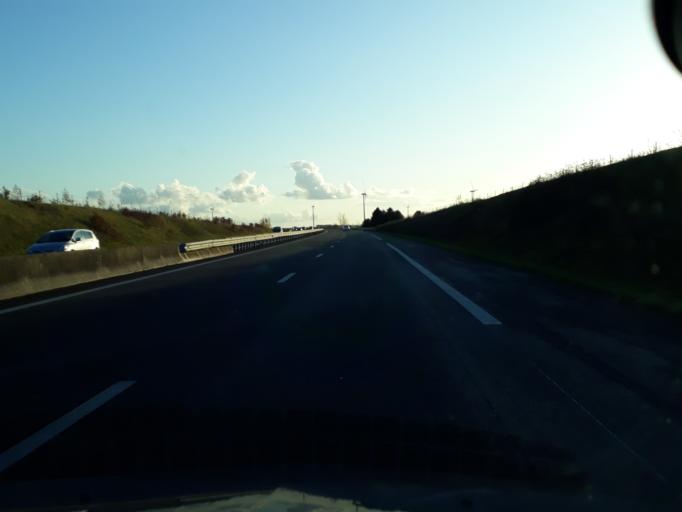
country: FR
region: Champagne-Ardenne
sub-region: Departement de l'Aube
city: Mailly-le-Camp
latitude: 48.6820
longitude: 4.1747
